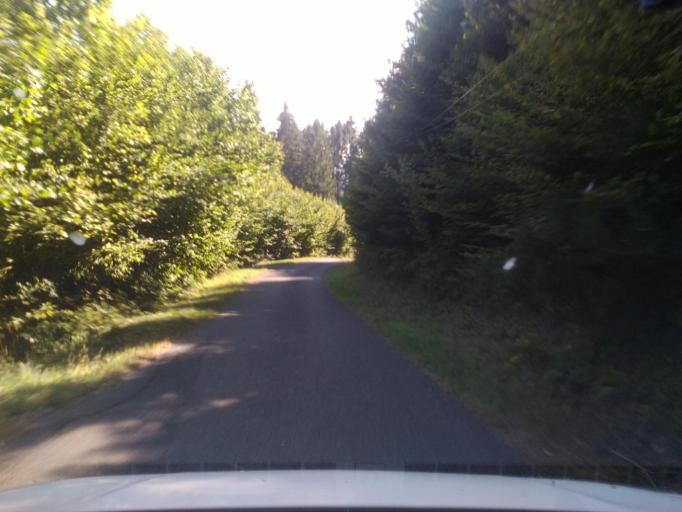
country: FR
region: Lorraine
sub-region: Departement des Vosges
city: Ban-de-Laveline
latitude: 48.3249
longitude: 7.0608
